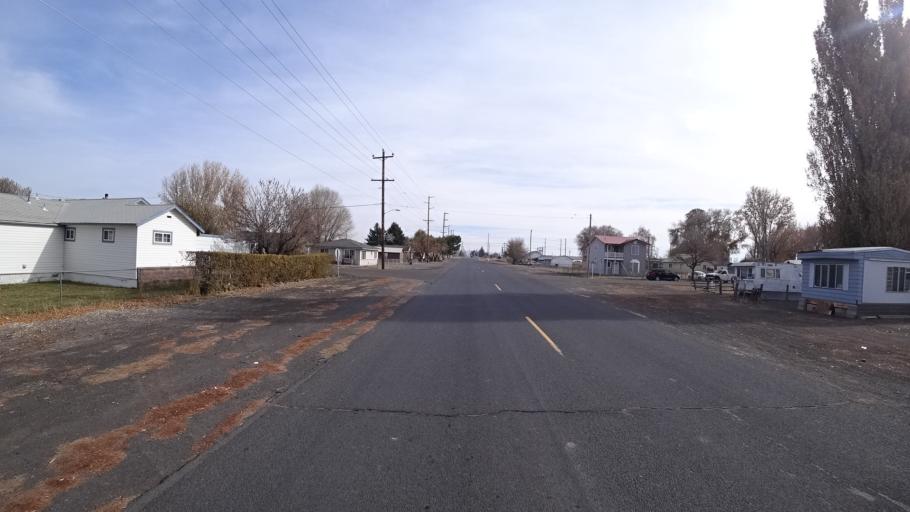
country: US
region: California
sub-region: Siskiyou County
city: Tulelake
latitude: 41.9537
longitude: -121.4744
